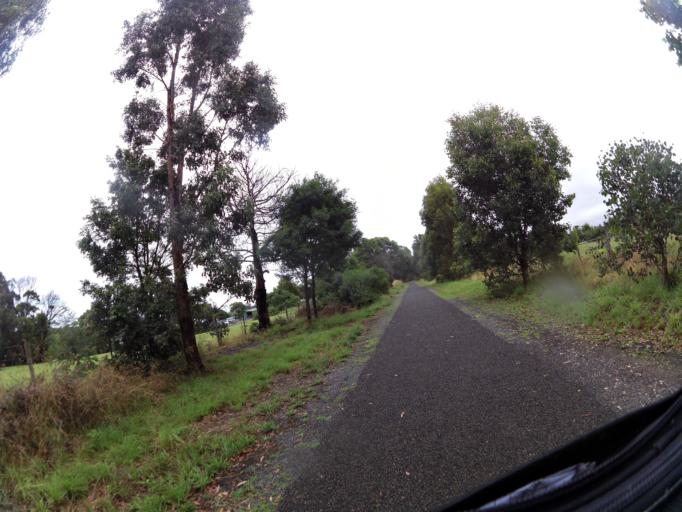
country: AU
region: Victoria
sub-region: East Gippsland
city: Bairnsdale
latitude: -37.8135
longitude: 147.7382
